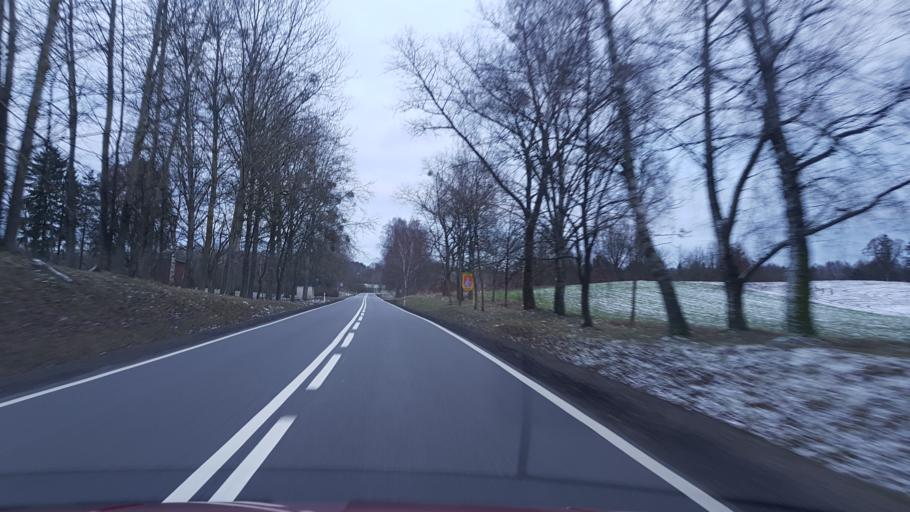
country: PL
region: Pomeranian Voivodeship
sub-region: Powiat bytowski
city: Tuchomie
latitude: 54.0501
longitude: 17.2149
